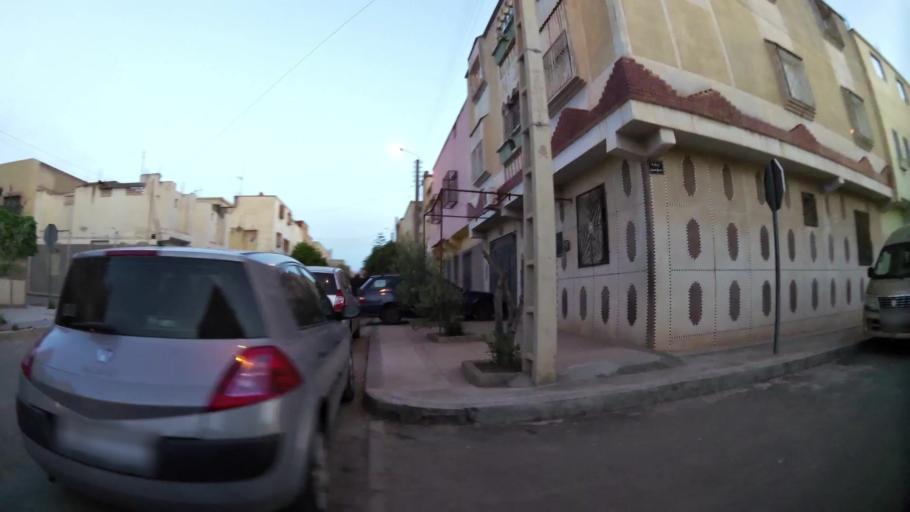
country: MA
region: Oriental
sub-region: Oujda-Angad
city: Oujda
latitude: 34.6844
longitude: -1.8775
